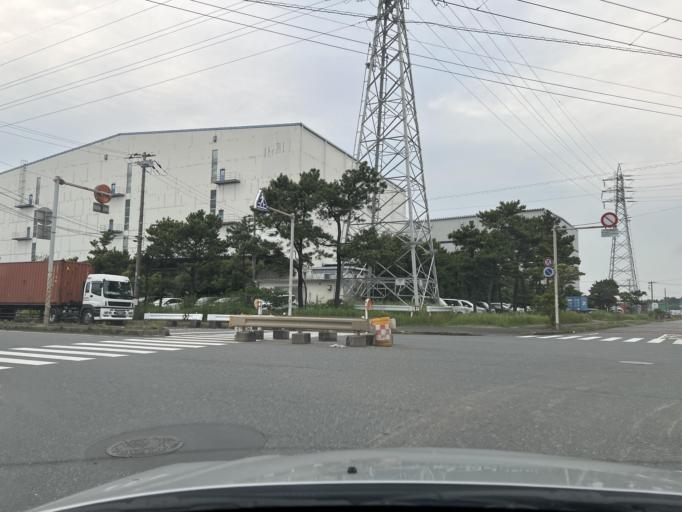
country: JP
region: Chiba
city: Funabashi
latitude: 35.6777
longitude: 139.9704
